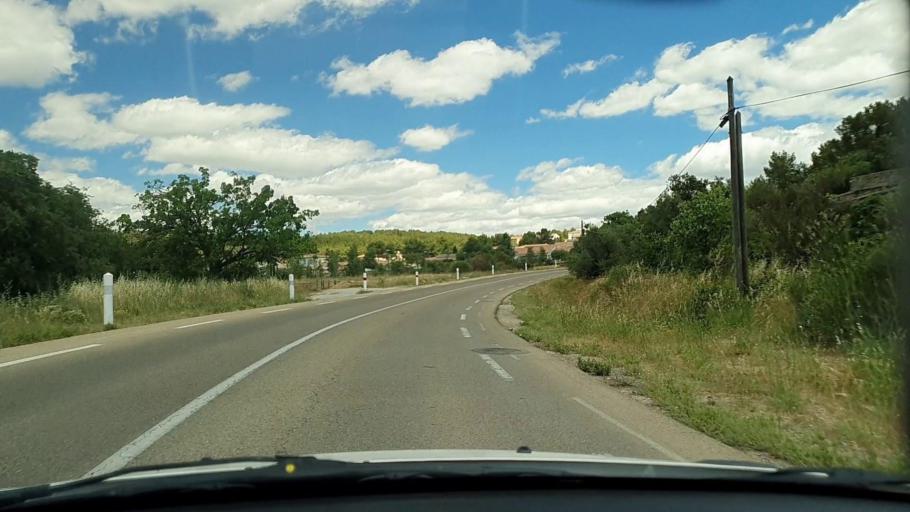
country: FR
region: Languedoc-Roussillon
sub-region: Departement du Gard
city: Poulx
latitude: 43.8707
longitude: 4.4086
